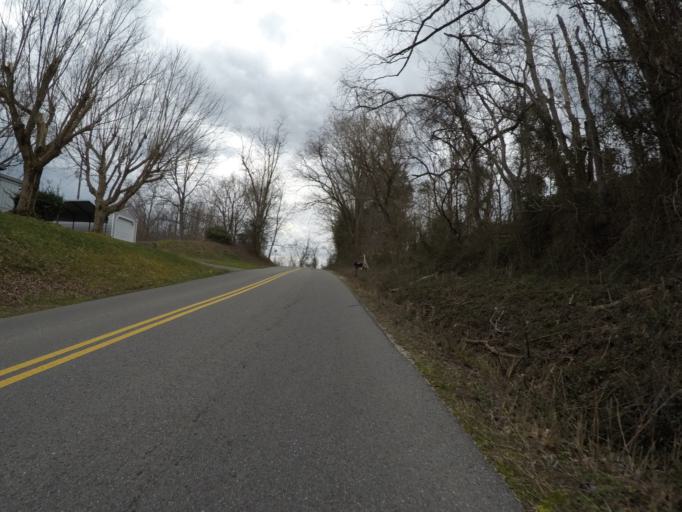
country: US
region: Ohio
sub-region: Lawrence County
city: Burlington
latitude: 38.4328
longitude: -82.5280
